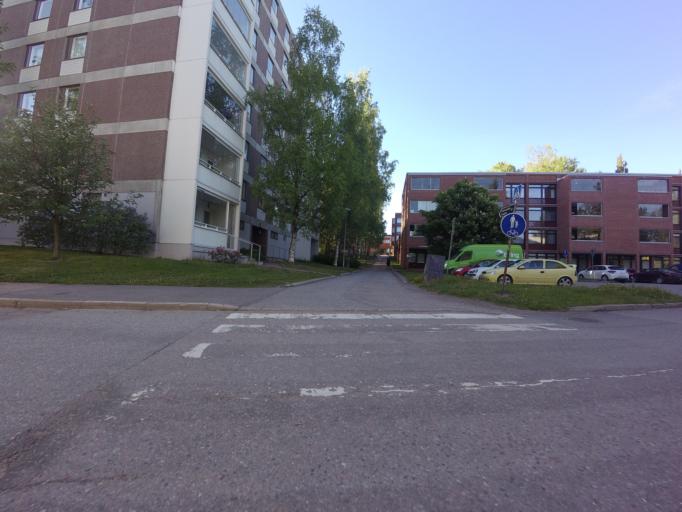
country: FI
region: Uusimaa
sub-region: Helsinki
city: Kauniainen
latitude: 60.1706
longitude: 24.7257
